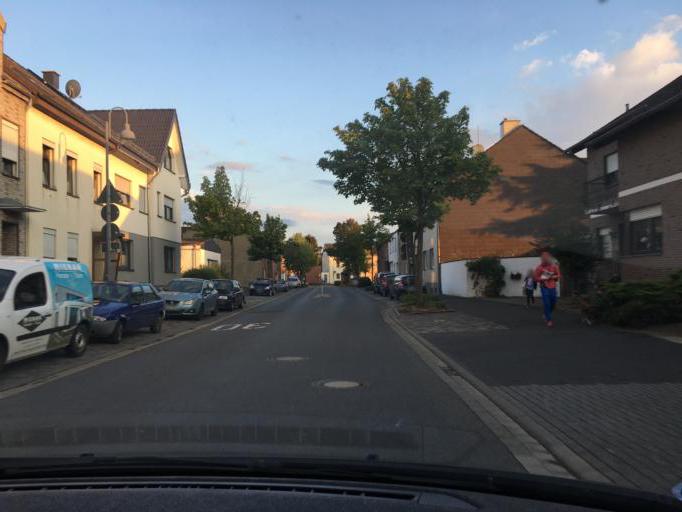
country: DE
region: North Rhine-Westphalia
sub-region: Regierungsbezirk Koln
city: Niederzier
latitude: 50.8539
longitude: 6.4586
